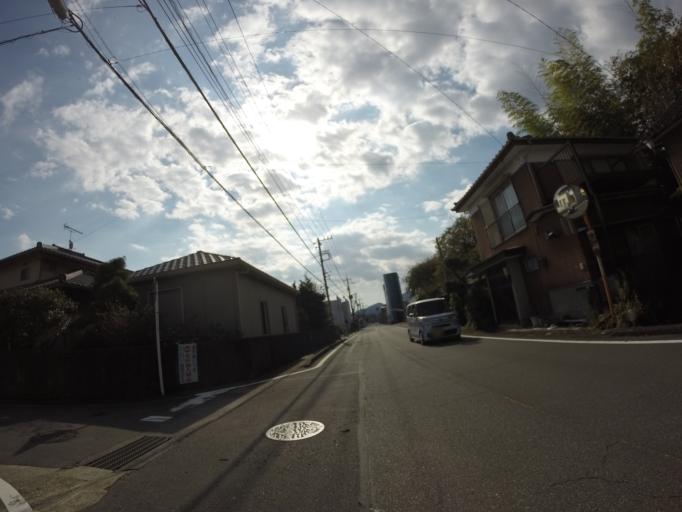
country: JP
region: Shizuoka
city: Fujinomiya
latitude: 35.1762
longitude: 138.6363
